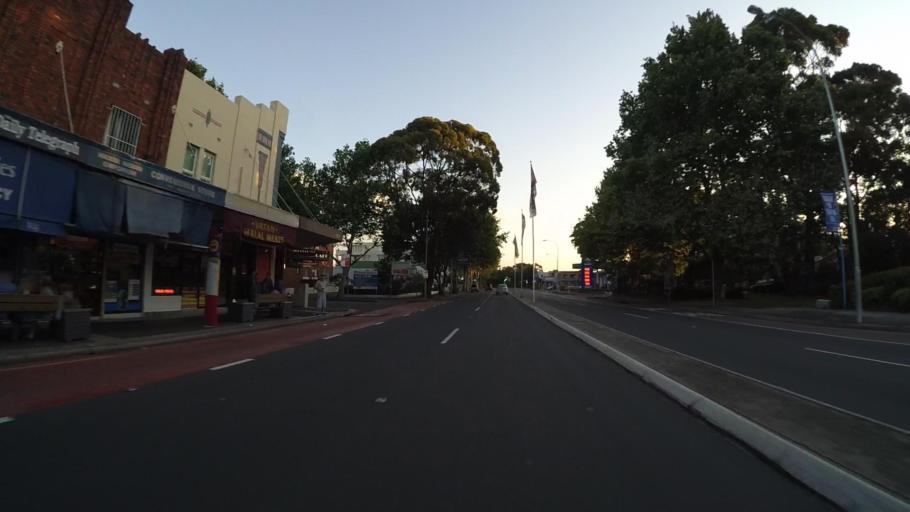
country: AU
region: New South Wales
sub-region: Botany Bay
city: Mascot
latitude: -33.9321
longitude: 151.1939
